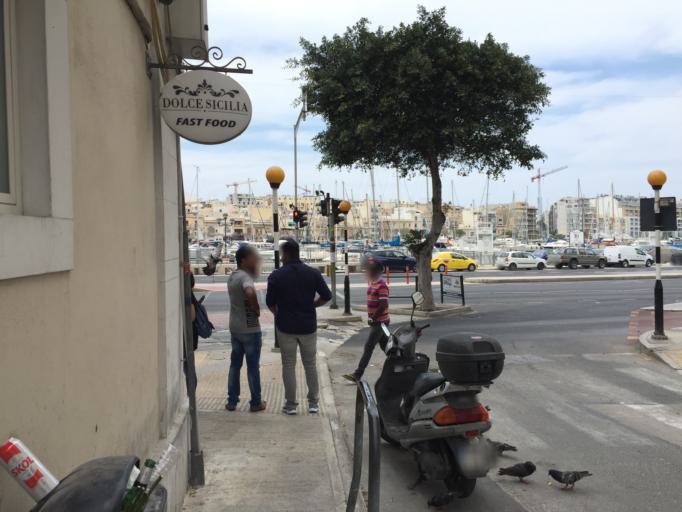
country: MT
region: Tal-Pieta
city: Pieta
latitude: 35.8945
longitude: 14.4911
